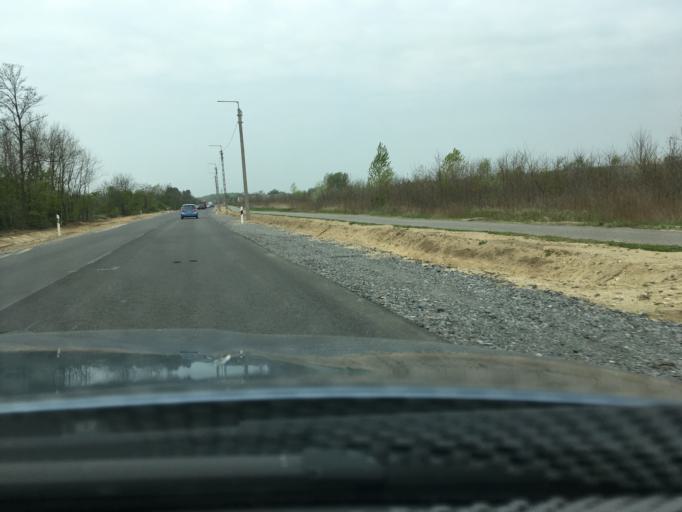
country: HU
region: Hajdu-Bihar
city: Nyiradony
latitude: 47.6671
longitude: 21.8487
